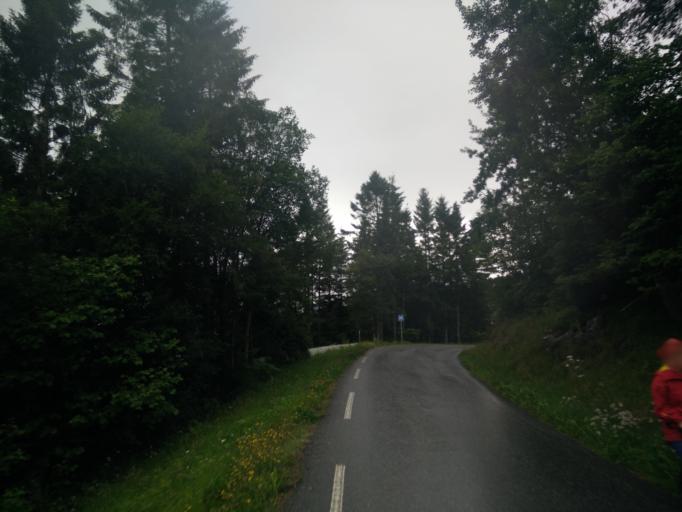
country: NO
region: More og Romsdal
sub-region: Kristiansund
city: Rensvik
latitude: 63.0173
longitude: 7.9036
